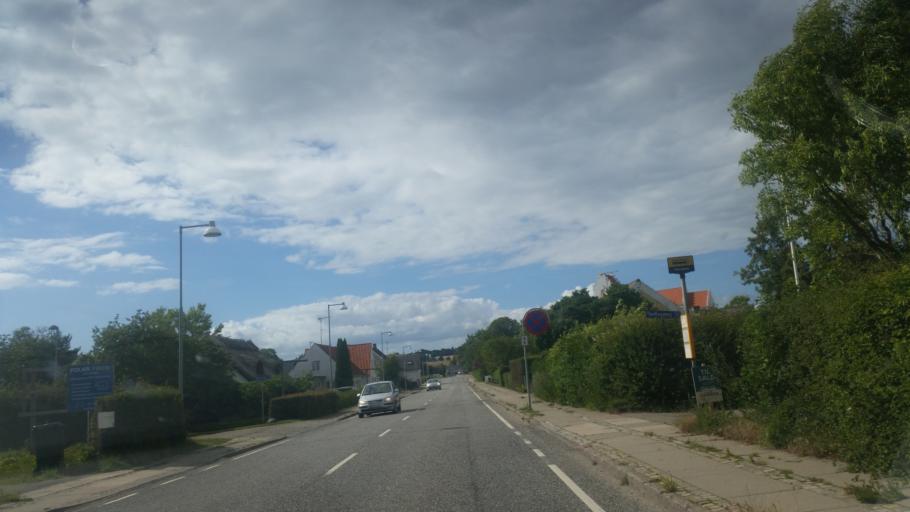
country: DK
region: Zealand
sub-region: Odsherred Kommune
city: Horve
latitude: 55.8007
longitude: 11.4442
